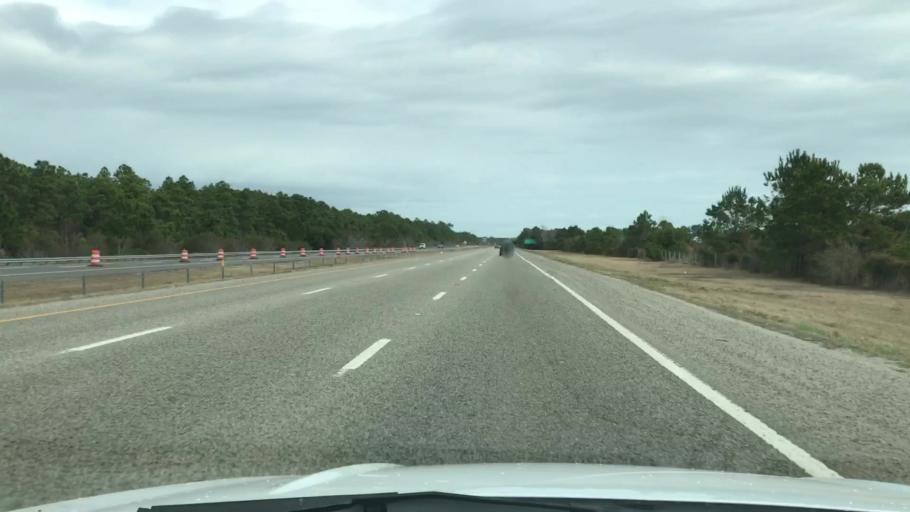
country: US
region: South Carolina
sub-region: Horry County
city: Socastee
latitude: 33.7135
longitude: -79.0048
